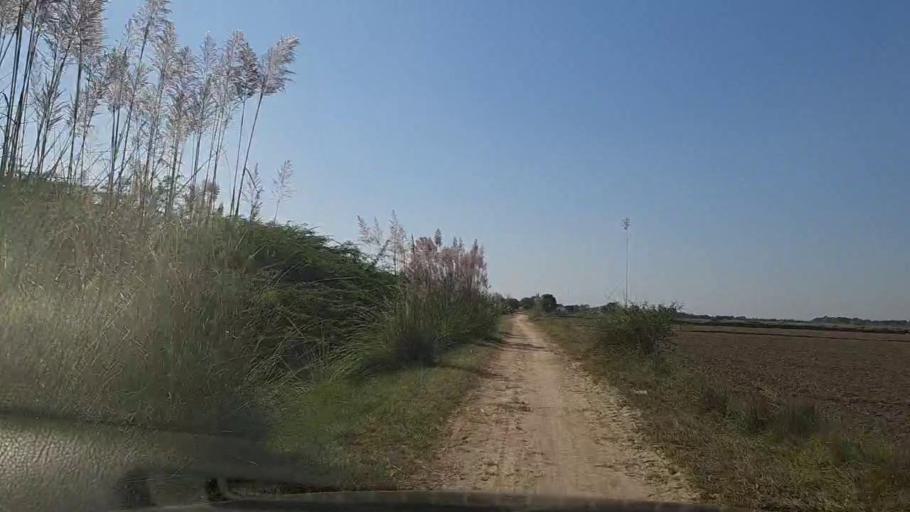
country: PK
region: Sindh
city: Mirpur Sakro
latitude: 24.5780
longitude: 67.7981
